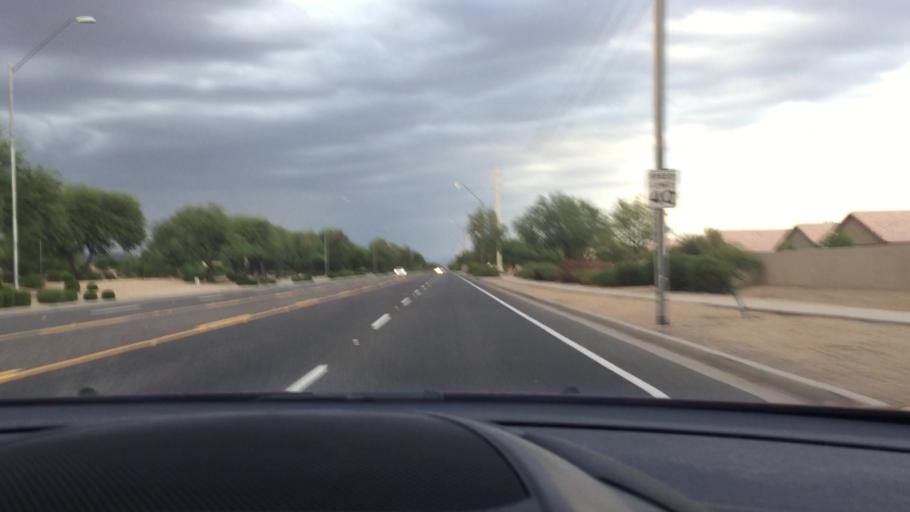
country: US
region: Arizona
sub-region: Maricopa County
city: Sun City
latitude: 33.6672
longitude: -112.2538
